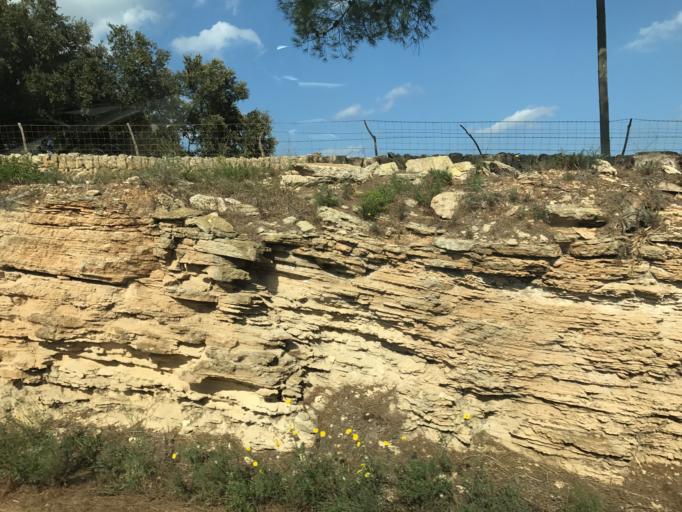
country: ES
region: Balearic Islands
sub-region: Illes Balears
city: Santa Margalida
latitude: 39.7280
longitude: 3.1974
